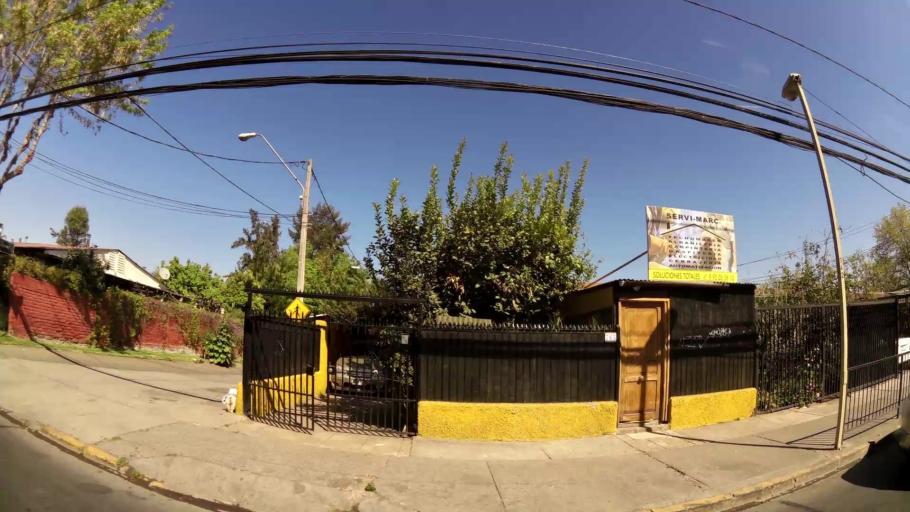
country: CL
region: Santiago Metropolitan
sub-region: Provincia de Santiago
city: Villa Presidente Frei, Nunoa, Santiago, Chile
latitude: -33.4123
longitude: -70.5355
